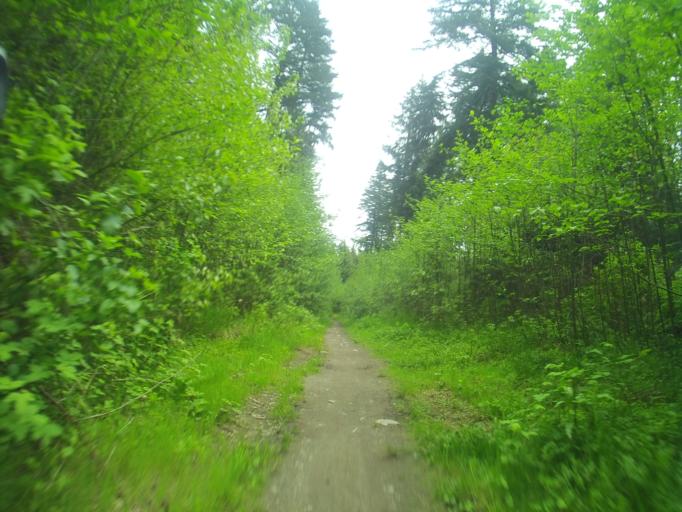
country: CA
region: British Columbia
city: West End
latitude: 49.2496
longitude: -123.2315
